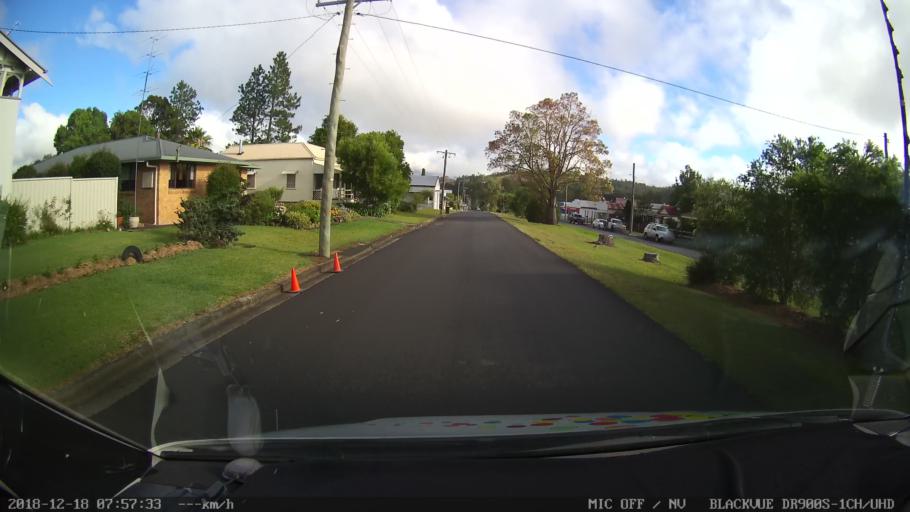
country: AU
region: New South Wales
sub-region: Kyogle
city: Kyogle
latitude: -28.3923
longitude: 152.6118
